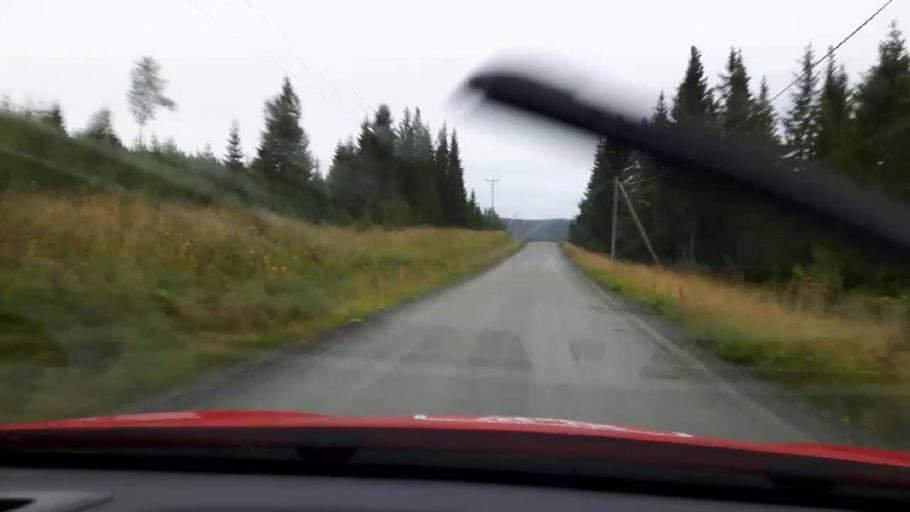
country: SE
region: Jaemtland
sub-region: Are Kommun
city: Are
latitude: 63.4171
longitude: 12.8265
